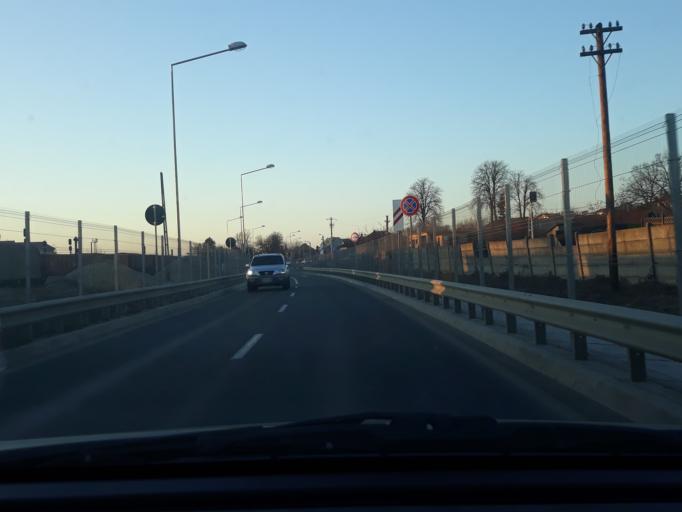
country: RO
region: Bihor
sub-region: Comuna Biharea
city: Oradea
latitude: 47.0755
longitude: 21.9336
